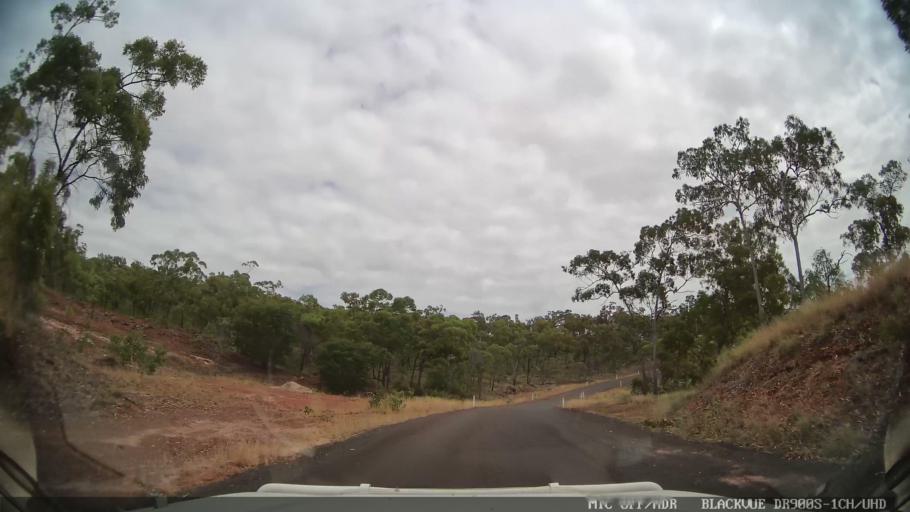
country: AU
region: Queensland
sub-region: Cook
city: Cooktown
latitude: -15.2831
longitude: 144.9102
